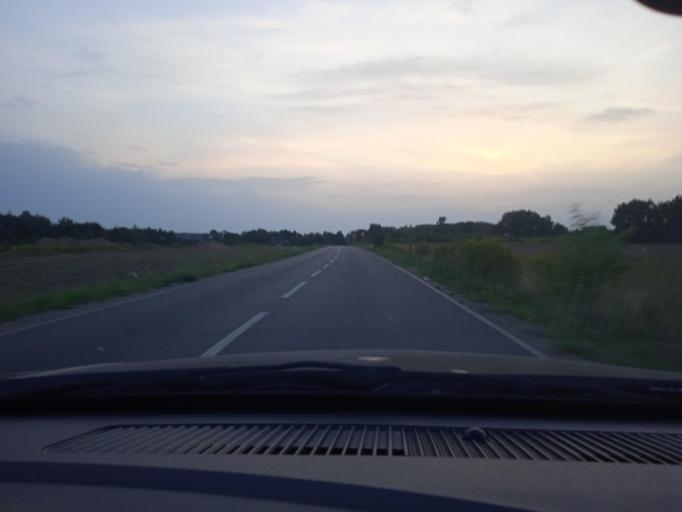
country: PL
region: Masovian Voivodeship
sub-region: Powiat nowodworski
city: Pomiechowek
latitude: 52.4648
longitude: 20.7048
